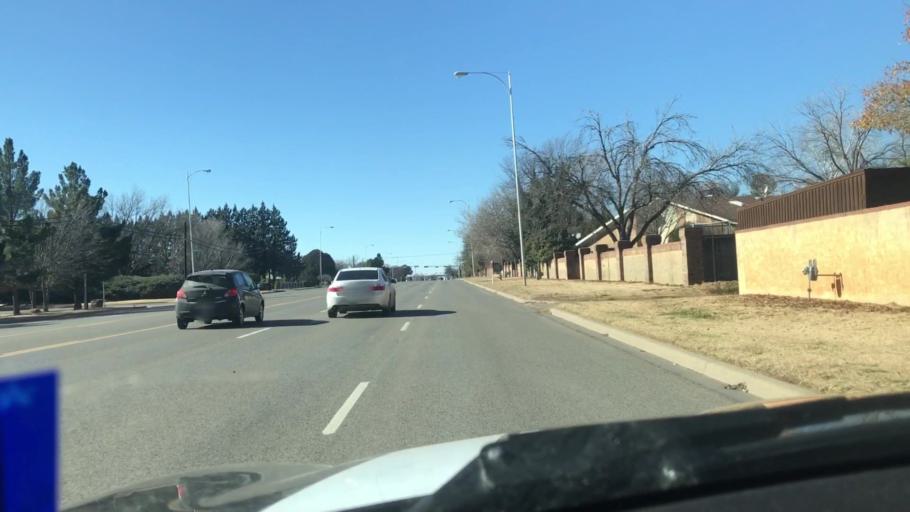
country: US
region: Texas
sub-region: Lubbock County
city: Lubbock
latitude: 33.5779
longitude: -101.9274
